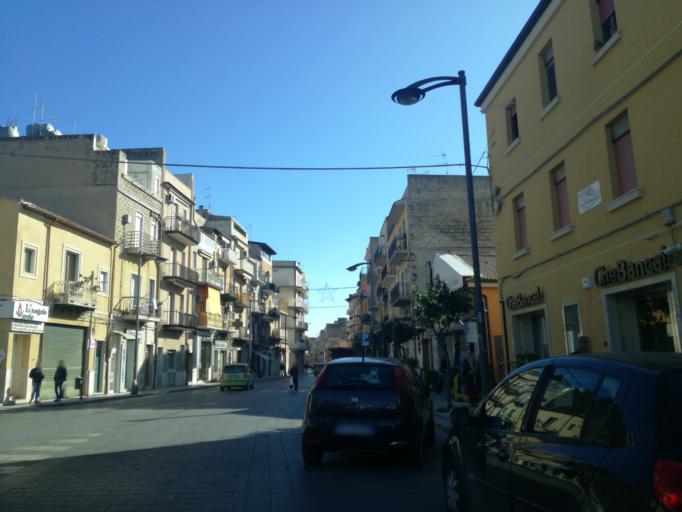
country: IT
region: Sicily
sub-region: Provincia di Caltanissetta
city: Gela
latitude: 37.0710
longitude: 14.2369
